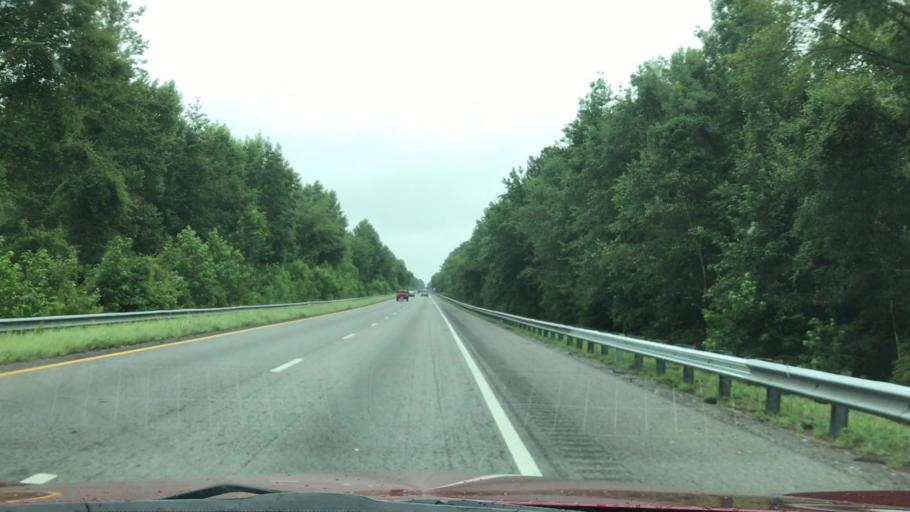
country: US
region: South Carolina
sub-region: Dorchester County
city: Ridgeville
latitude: 33.1523
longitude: -80.3424
